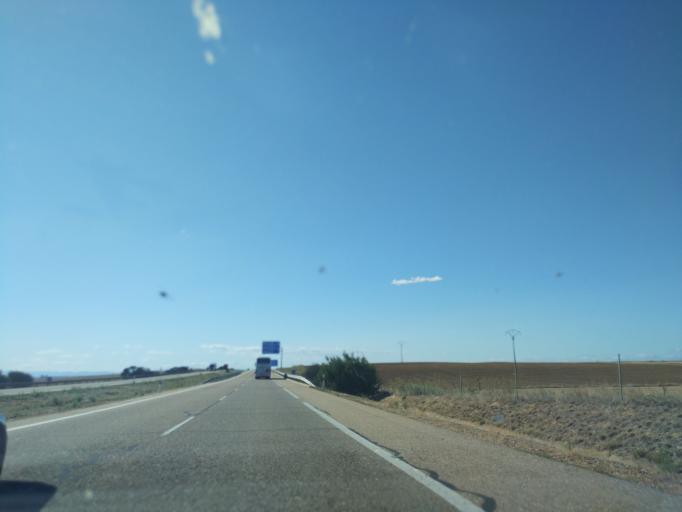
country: ES
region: Castille and Leon
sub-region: Provincia de Zamora
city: San Esteban del Molar
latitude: 41.9551
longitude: -5.5737
